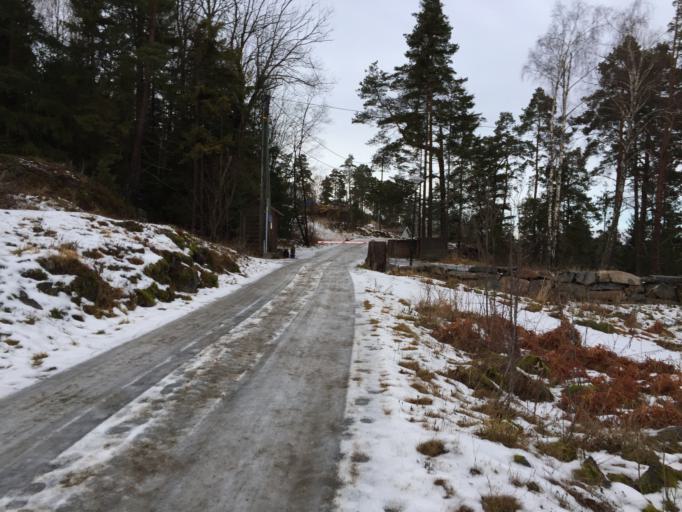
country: NO
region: Ostfold
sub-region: Moss
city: Moss
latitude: 59.4871
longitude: 10.6727
